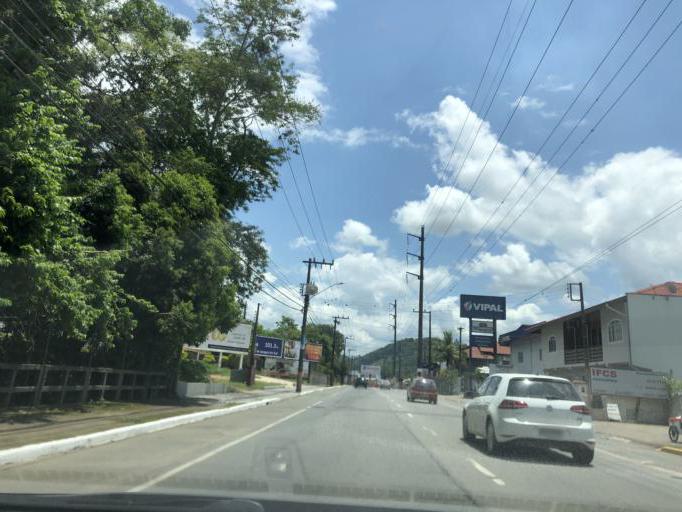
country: BR
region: Santa Catarina
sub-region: Jaragua Do Sul
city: Jaragua do Sul
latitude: -26.5100
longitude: -49.1094
